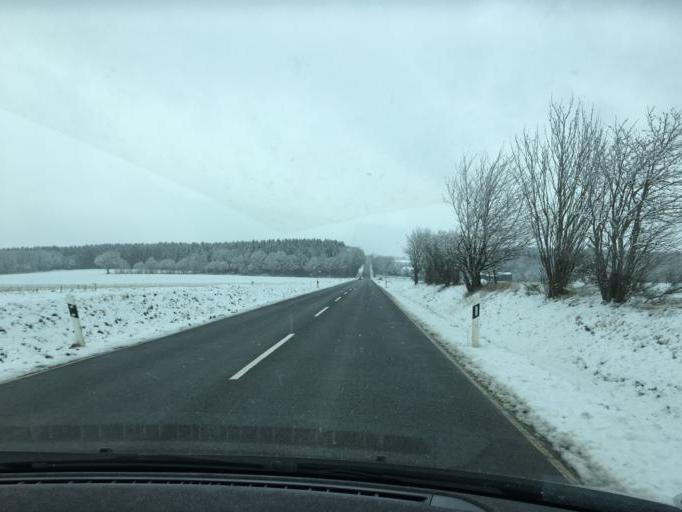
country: DE
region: North Rhine-Westphalia
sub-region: Regierungsbezirk Koln
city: Hurtgenwald
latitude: 50.7098
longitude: 6.4015
